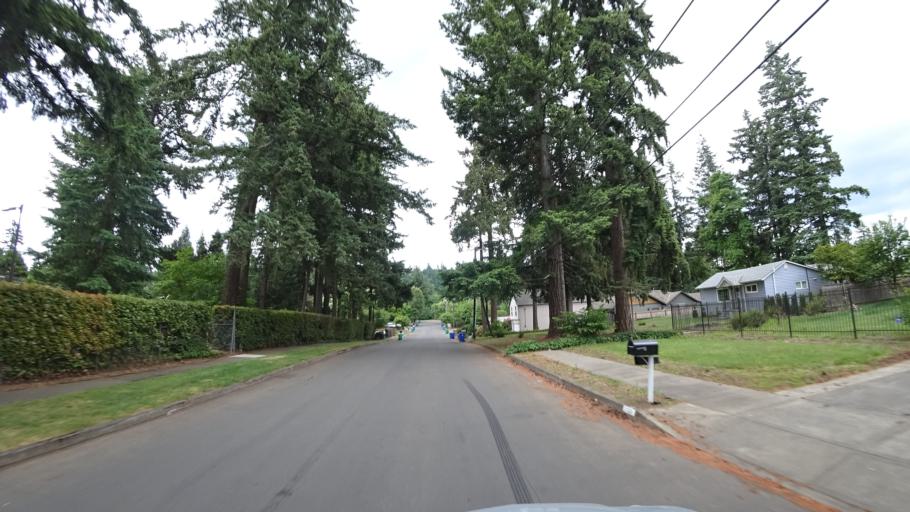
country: US
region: Oregon
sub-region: Clackamas County
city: Happy Valley
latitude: 45.4985
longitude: -122.5060
